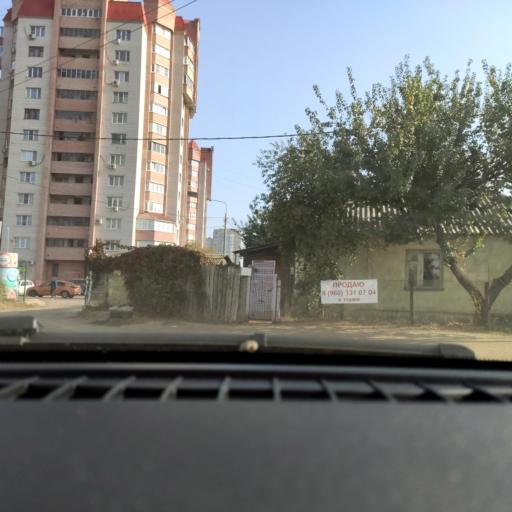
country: RU
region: Voronezj
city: Voronezh
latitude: 51.6534
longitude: 39.2382
